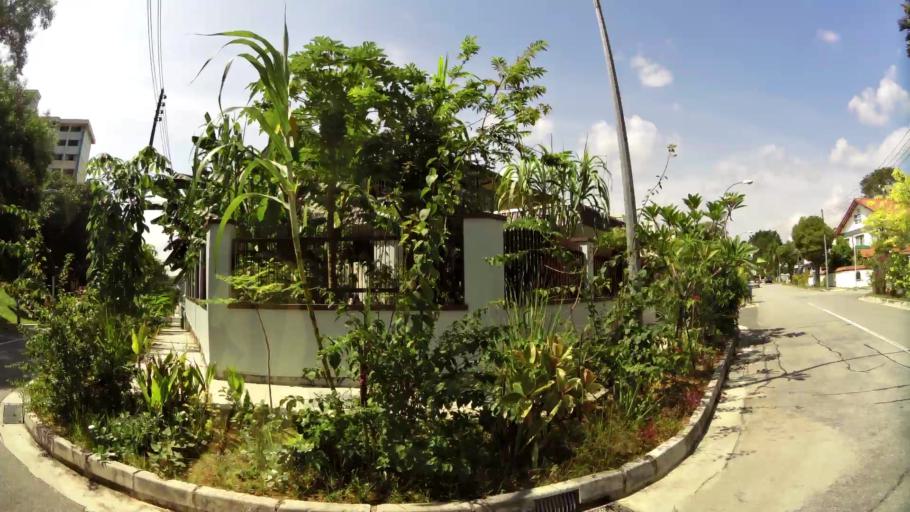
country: SG
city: Singapore
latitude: 1.3724
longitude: 103.8411
